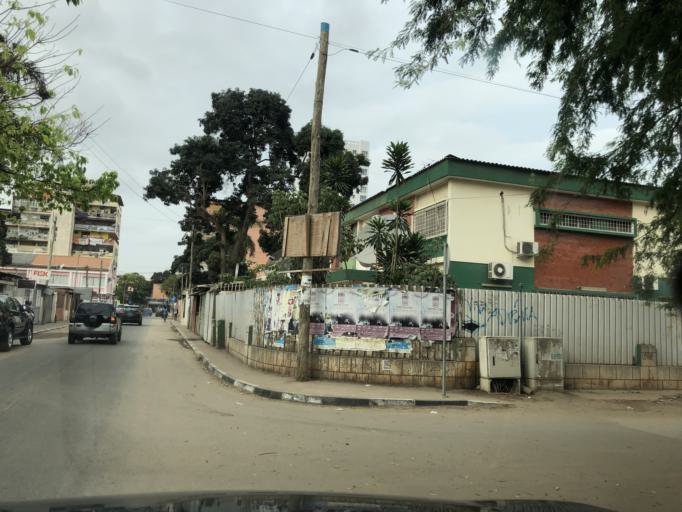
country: AO
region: Luanda
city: Luanda
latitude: -8.8202
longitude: 13.2503
